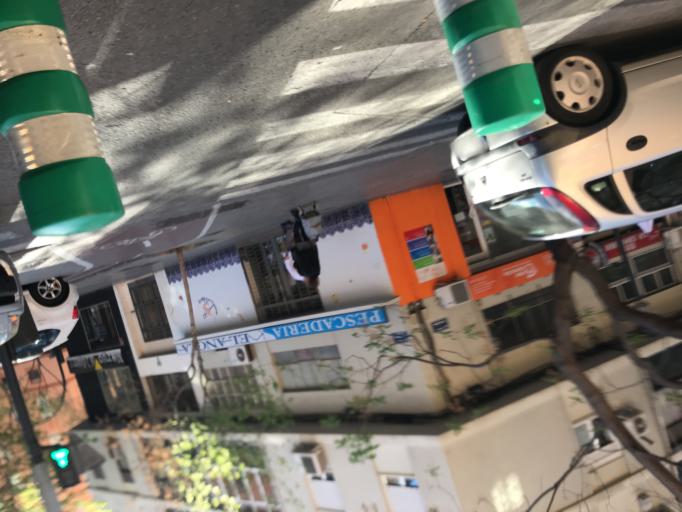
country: ES
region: Valencia
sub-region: Provincia de Valencia
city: Valencia
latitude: 39.4676
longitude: -0.3852
